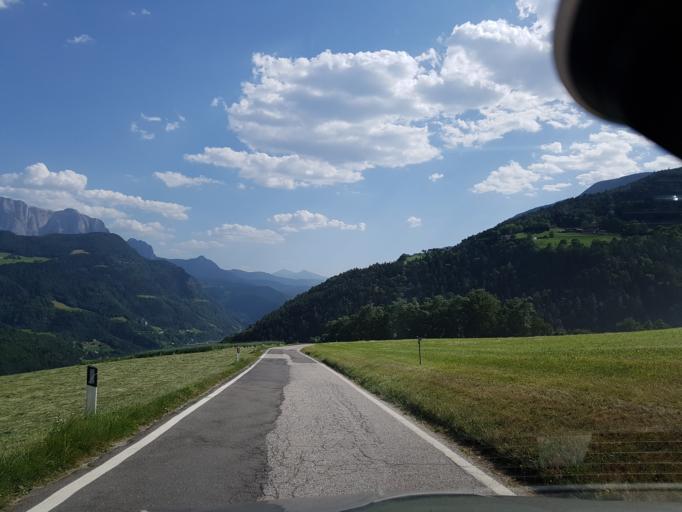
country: IT
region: Trentino-Alto Adige
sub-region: Bolzano
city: Villandro - Villanders
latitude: 46.6224
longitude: 11.5319
